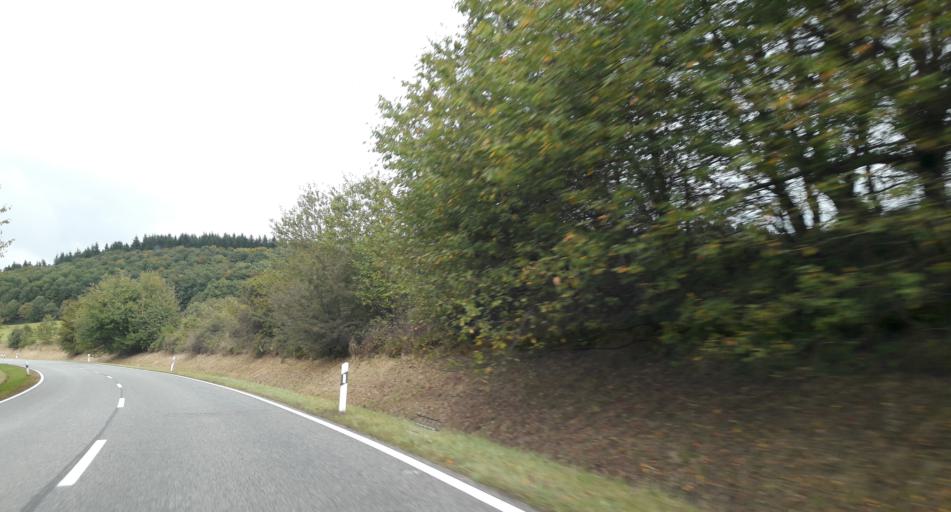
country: DE
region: Saarland
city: Freisen
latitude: 49.5285
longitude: 7.2275
